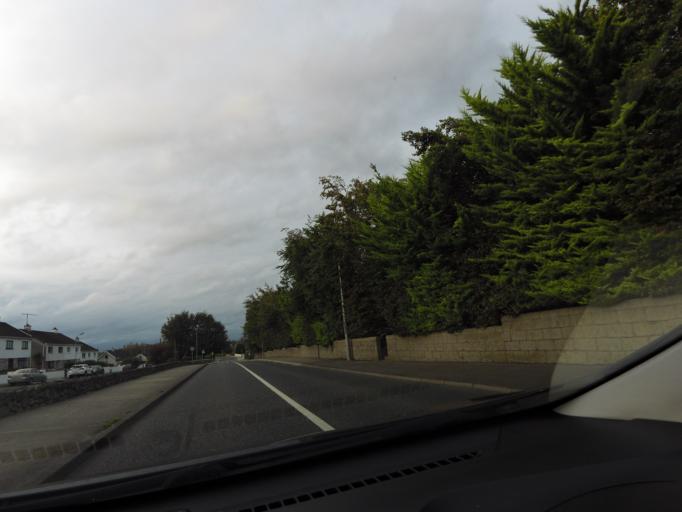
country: IE
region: Leinster
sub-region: An Iarmhi
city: Athlone
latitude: 53.4206
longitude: -7.9009
